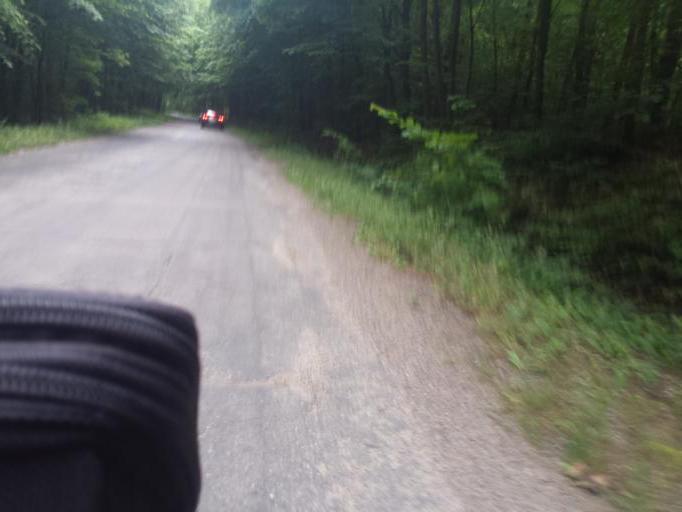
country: PL
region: Warmian-Masurian Voivodeship
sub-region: Powiat ilawski
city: Ilawa
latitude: 53.5451
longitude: 19.5587
